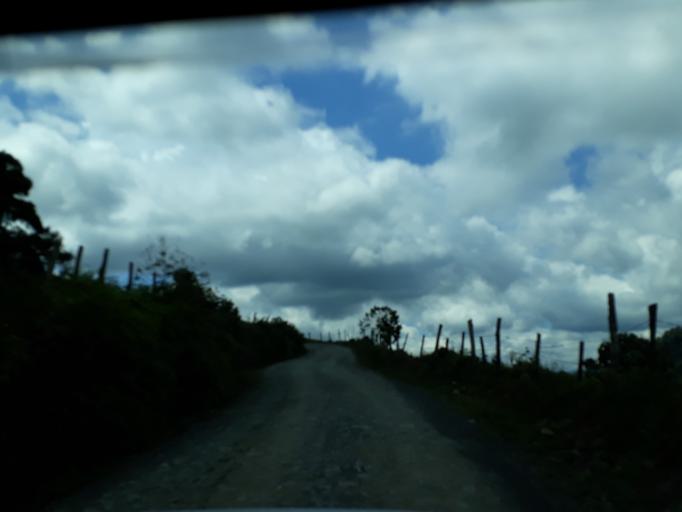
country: CO
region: Cundinamarca
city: Topaipi
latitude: 5.2908
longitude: -74.1950
